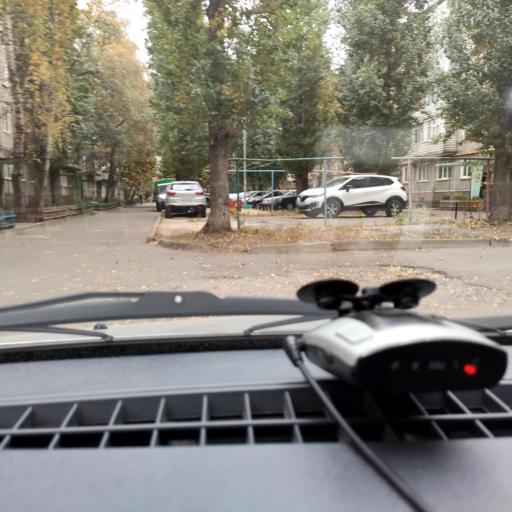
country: RU
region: Voronezj
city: Voronezh
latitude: 51.6513
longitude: 39.2374
